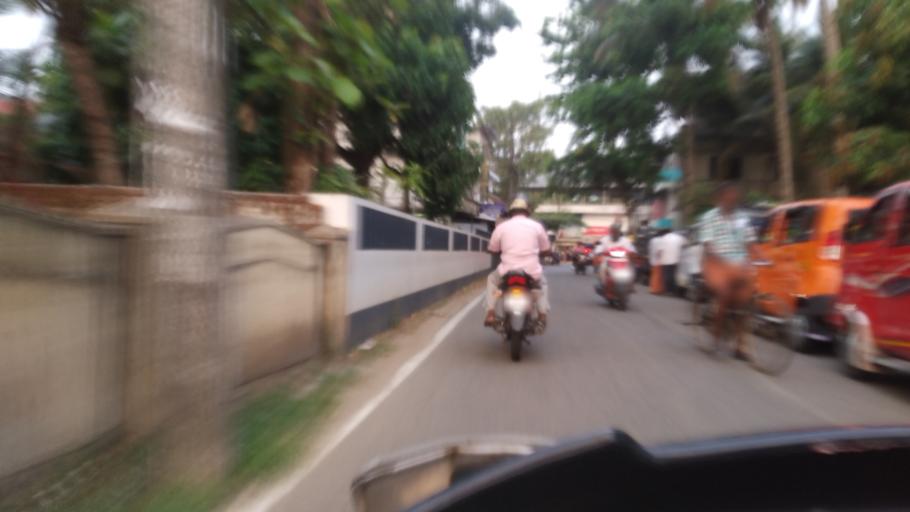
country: IN
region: Kerala
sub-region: Thrissur District
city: Kodungallur
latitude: 10.1587
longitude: 76.2126
